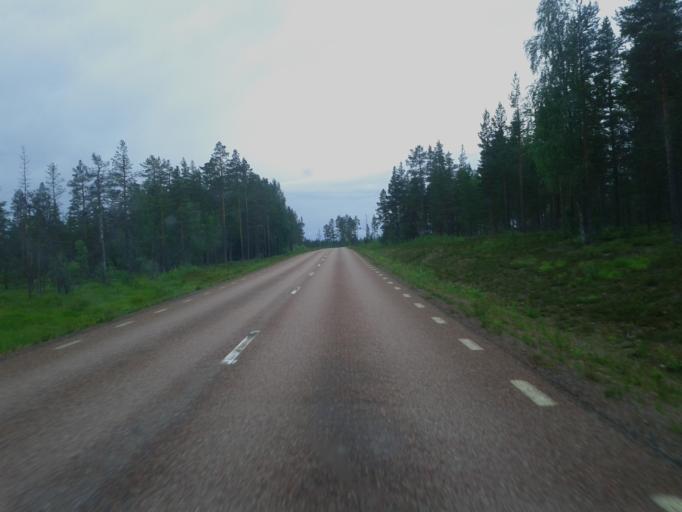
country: SE
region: Dalarna
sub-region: Alvdalens Kommun
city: AElvdalen
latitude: 61.4722
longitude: 13.4229
